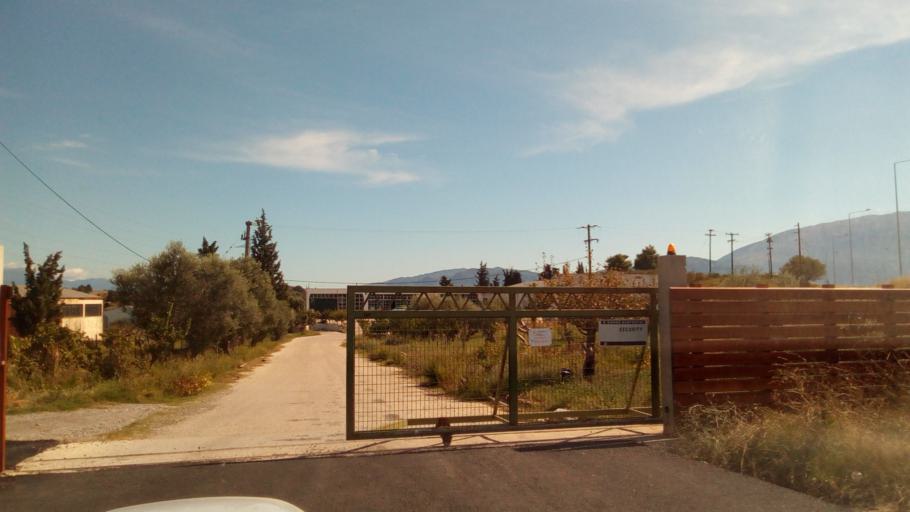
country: GR
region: West Greece
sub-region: Nomos Aitolias kai Akarnanias
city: Antirrio
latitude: 38.3454
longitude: 21.7559
